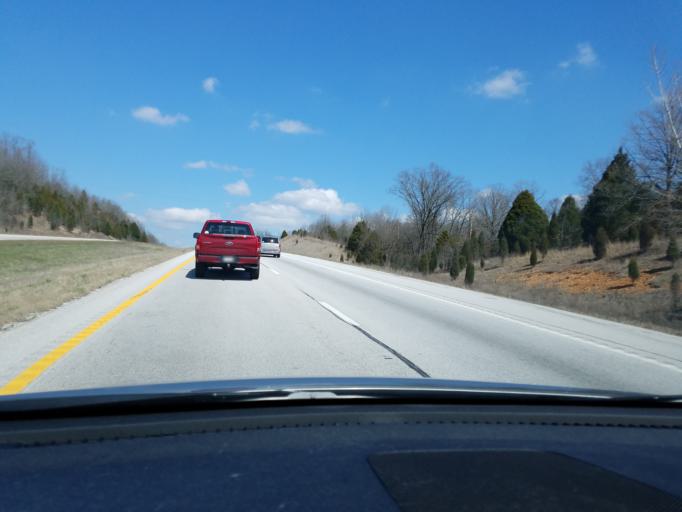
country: US
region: Missouri
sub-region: Christian County
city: Ozark
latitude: 36.8731
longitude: -93.2306
